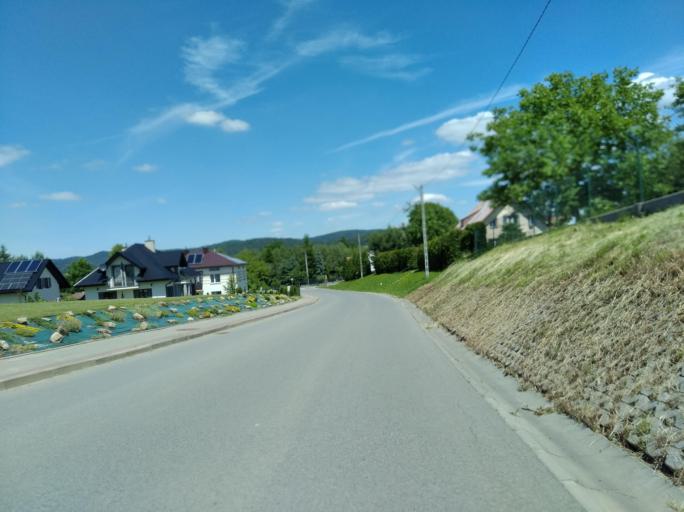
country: PL
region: Subcarpathian Voivodeship
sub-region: Powiat krosnienski
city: Wojaszowka
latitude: 49.7782
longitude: 21.6721
